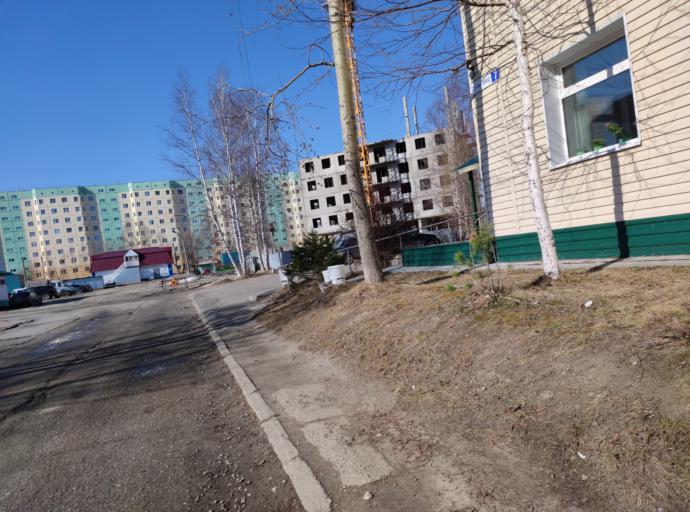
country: RU
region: Khanty-Mansiyskiy Avtonomnyy Okrug
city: Langepas
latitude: 61.2511
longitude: 75.1675
